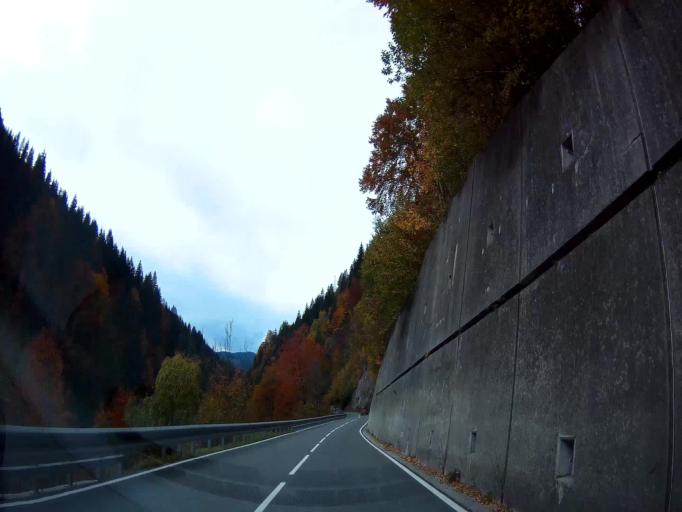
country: AT
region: Salzburg
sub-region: Politischer Bezirk Sankt Johann im Pongau
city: Bischofshofen
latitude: 47.3976
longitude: 13.1942
